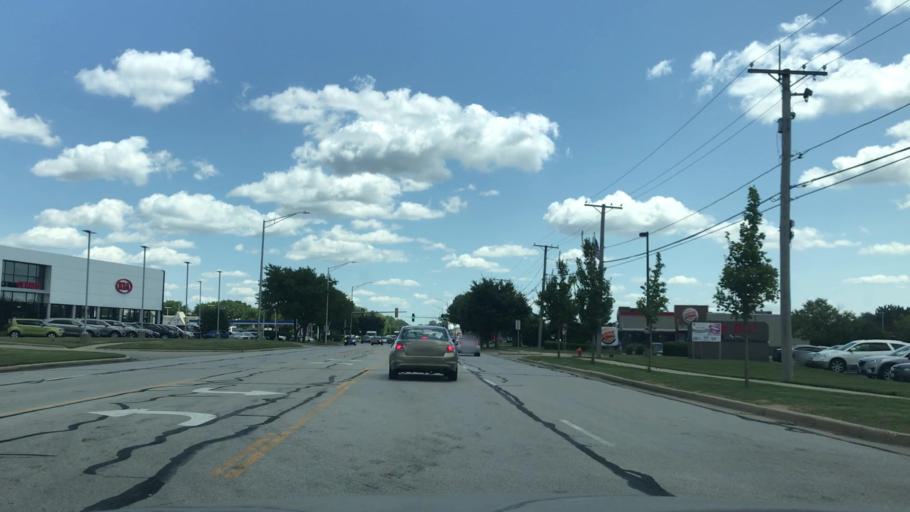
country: US
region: Illinois
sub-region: DuPage County
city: Naperville
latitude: 41.7643
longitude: -88.1887
